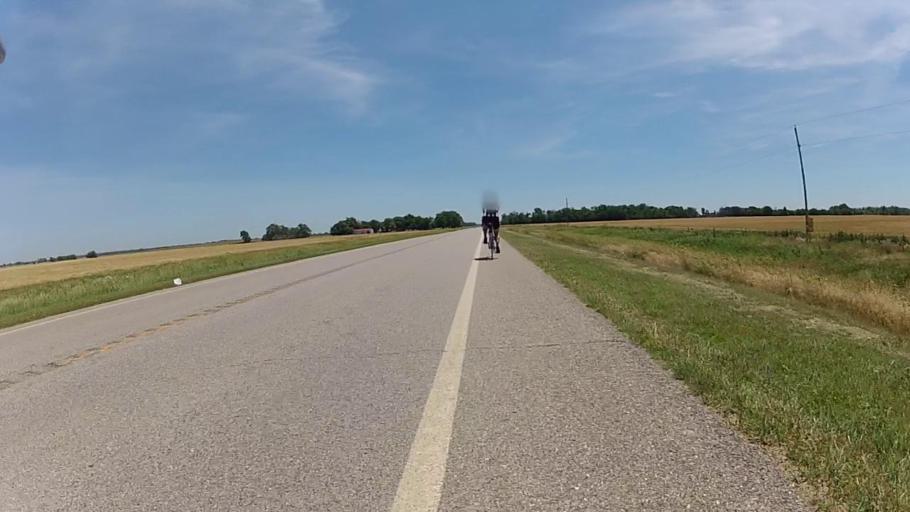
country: US
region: Kansas
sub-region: Barber County
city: Medicine Lodge
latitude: 37.2534
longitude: -98.4385
